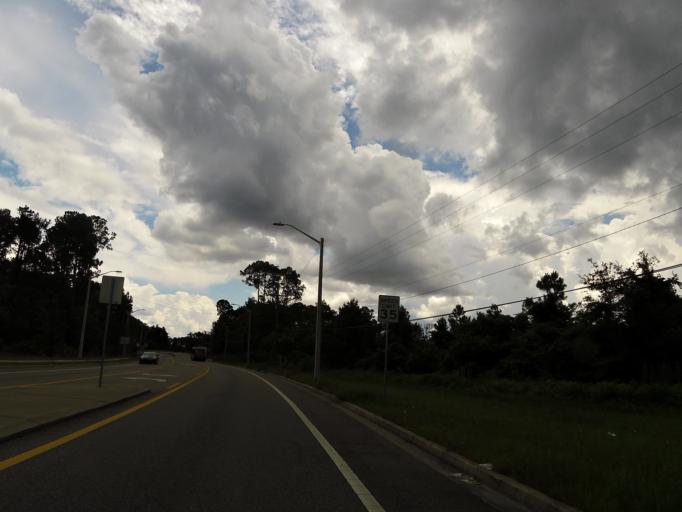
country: US
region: Florida
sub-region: Duval County
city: Jacksonville
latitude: 30.4120
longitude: -81.6612
